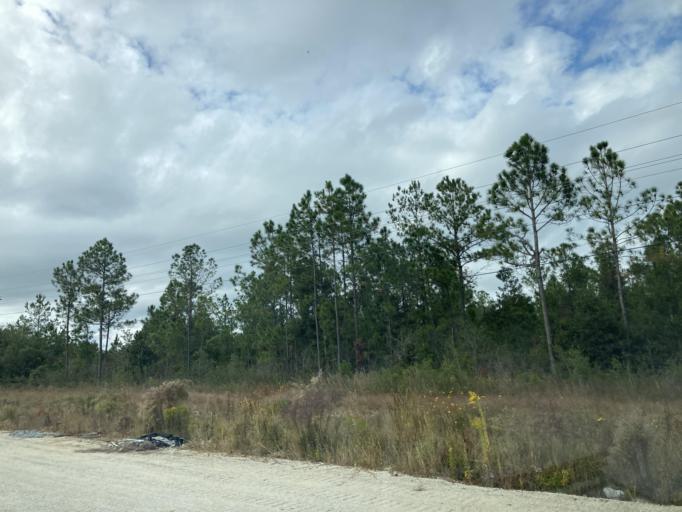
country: US
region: Mississippi
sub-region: Jackson County
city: Gulf Hills
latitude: 30.4390
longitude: -88.8172
